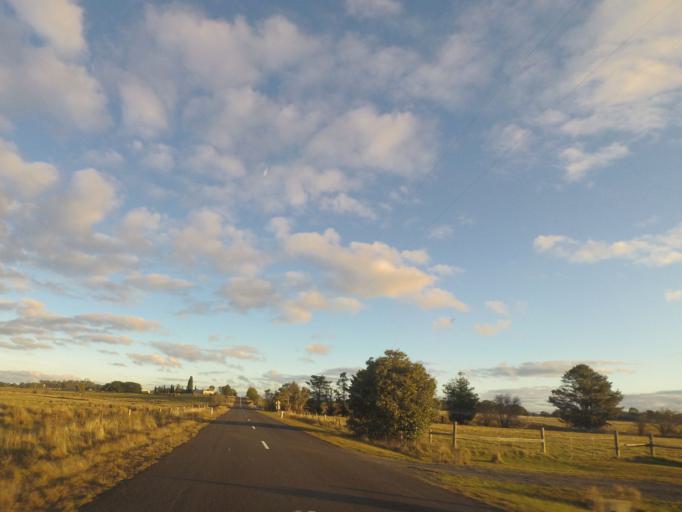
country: AU
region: Victoria
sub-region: Mount Alexander
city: Castlemaine
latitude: -37.2808
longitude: 144.5123
